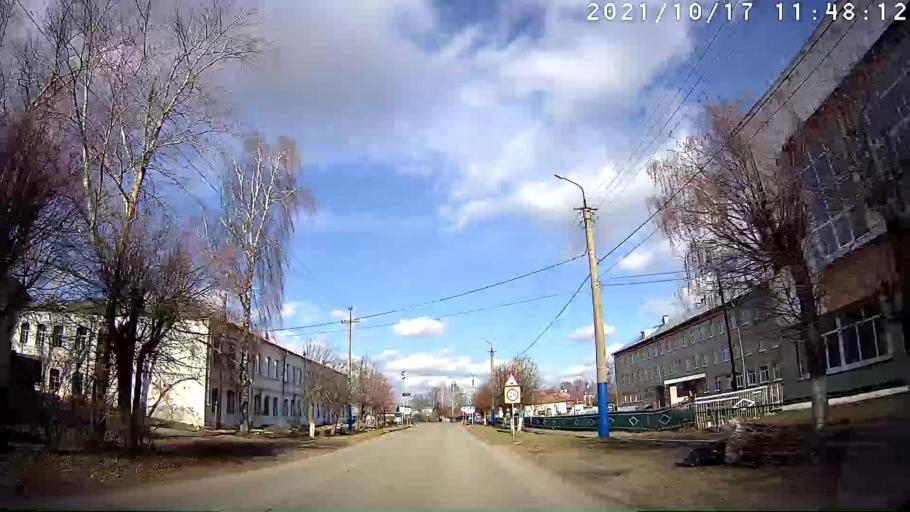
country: RU
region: Mariy-El
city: Kuzhener
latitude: 57.0024
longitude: 48.7338
